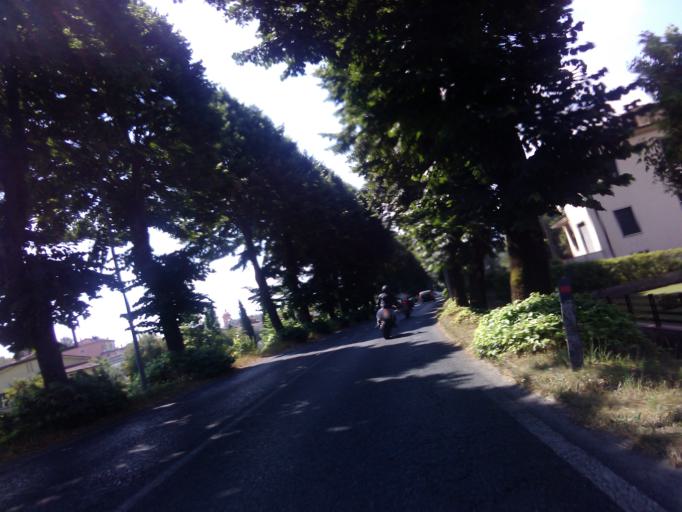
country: IT
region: Tuscany
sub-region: Provincia di Lucca
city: Lucca
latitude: 43.8557
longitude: 10.4455
